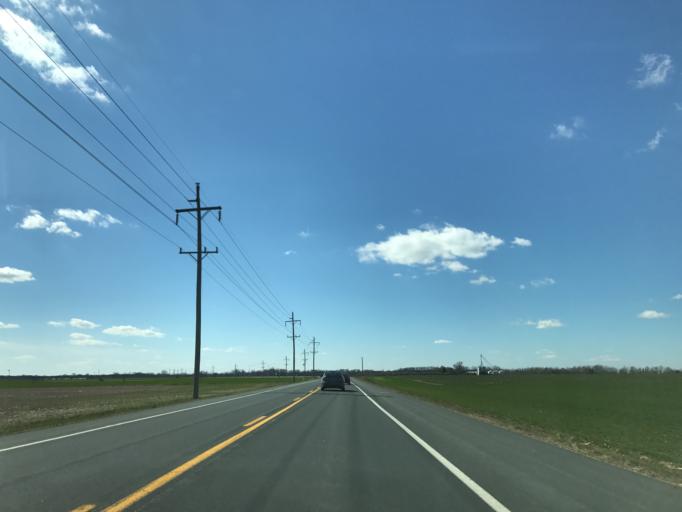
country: US
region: Maryland
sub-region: Queen Anne's County
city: Kingstown
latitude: 39.2620
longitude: -75.9195
